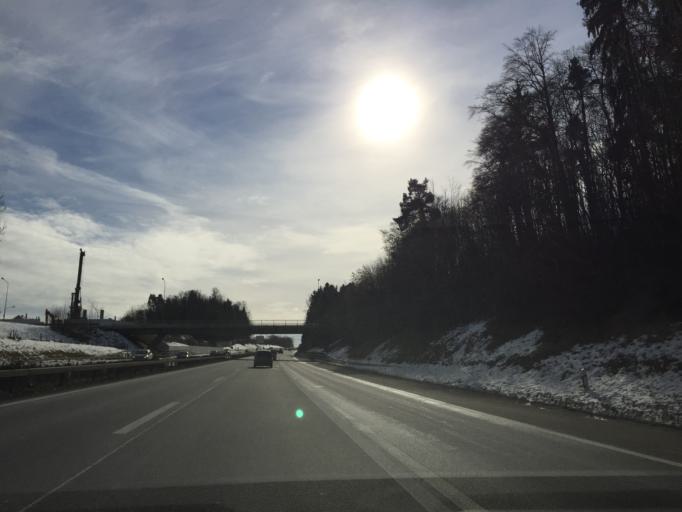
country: CH
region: Zurich
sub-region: Bezirk Horgen
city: Ruschlikon
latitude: 47.2994
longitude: 8.5485
